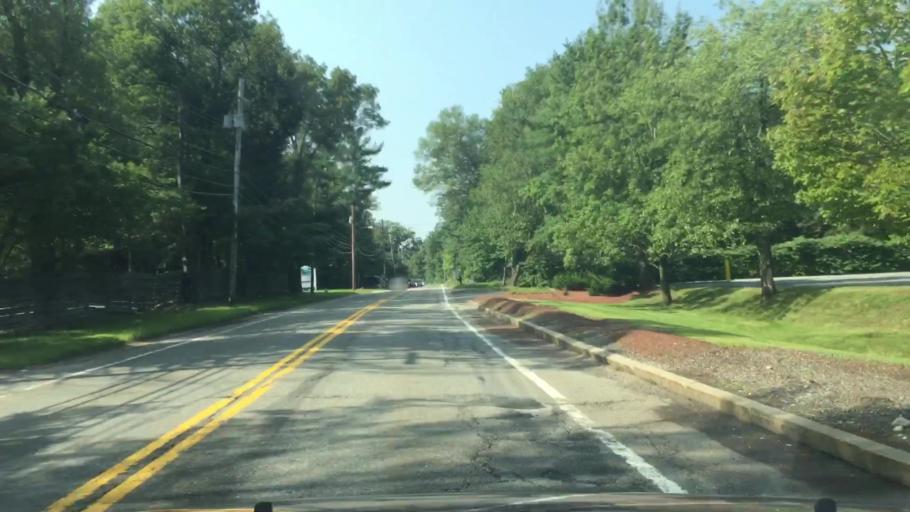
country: US
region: Massachusetts
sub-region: Middlesex County
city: Westford
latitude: 42.5597
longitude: -71.4347
